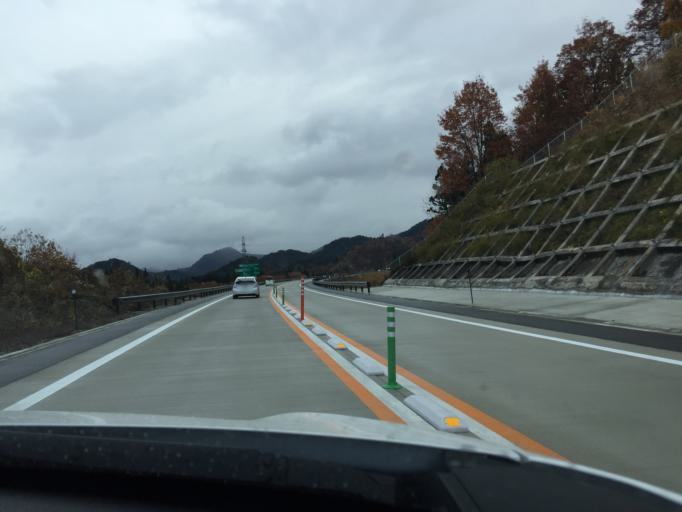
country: JP
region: Yamagata
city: Yonezawa
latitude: 37.8908
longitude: 140.1693
